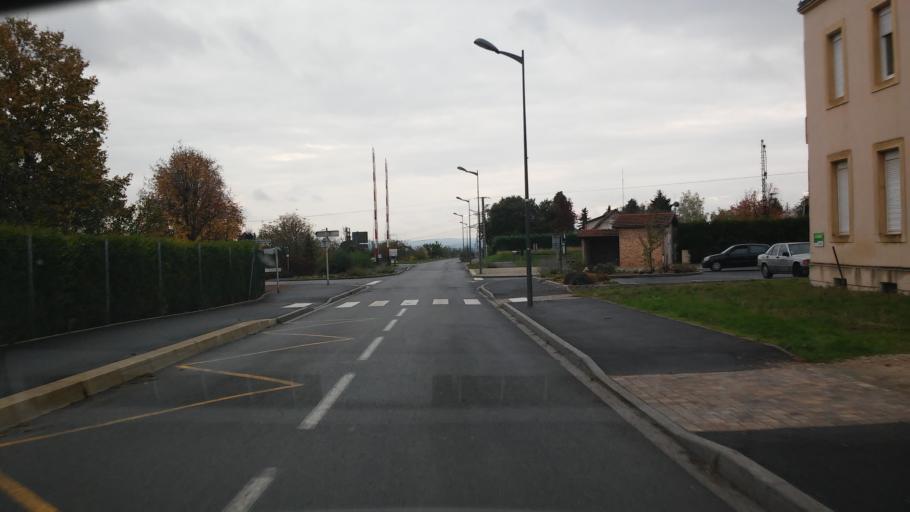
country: FR
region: Lorraine
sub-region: Departement de la Moselle
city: Vigy
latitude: 49.2052
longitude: 6.2924
